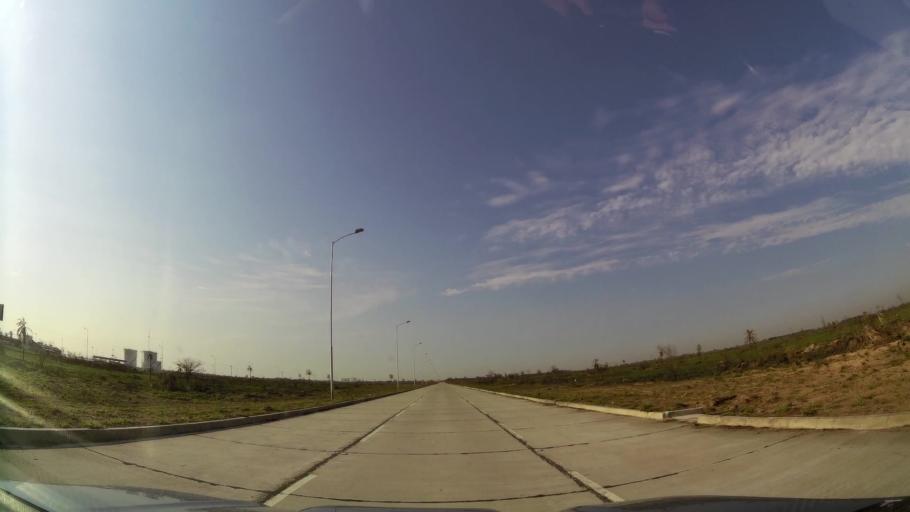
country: BO
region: Santa Cruz
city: La Belgica
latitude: -17.6554
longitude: -63.1390
